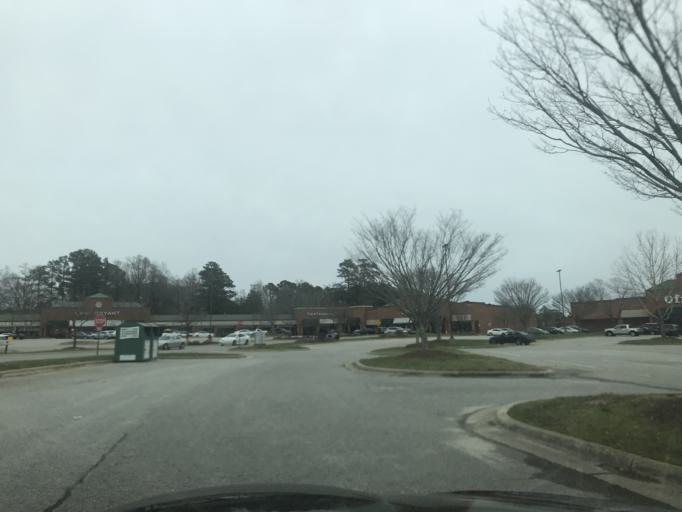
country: US
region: North Carolina
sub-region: Wake County
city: Garner
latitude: 35.7143
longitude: -78.6377
